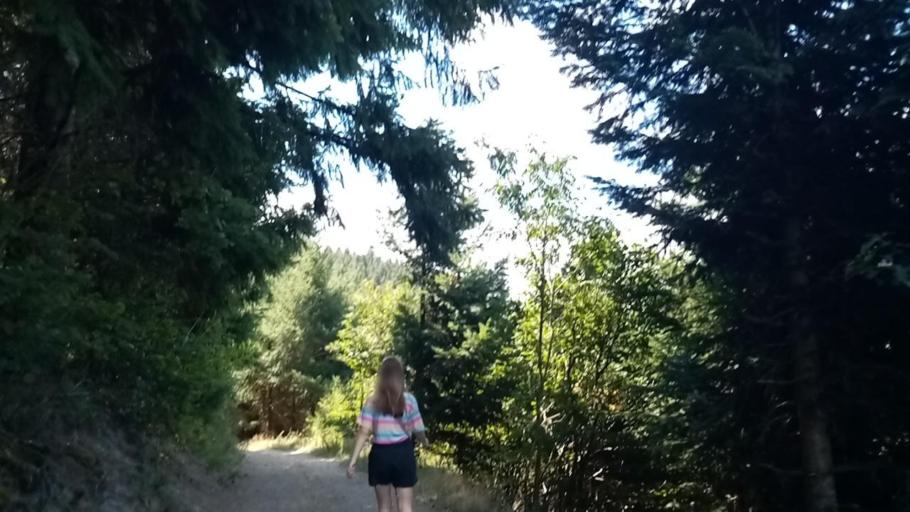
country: FR
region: Rhone-Alpes
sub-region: Departement du Rhone
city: Grandris
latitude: 46.0097
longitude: 4.5441
